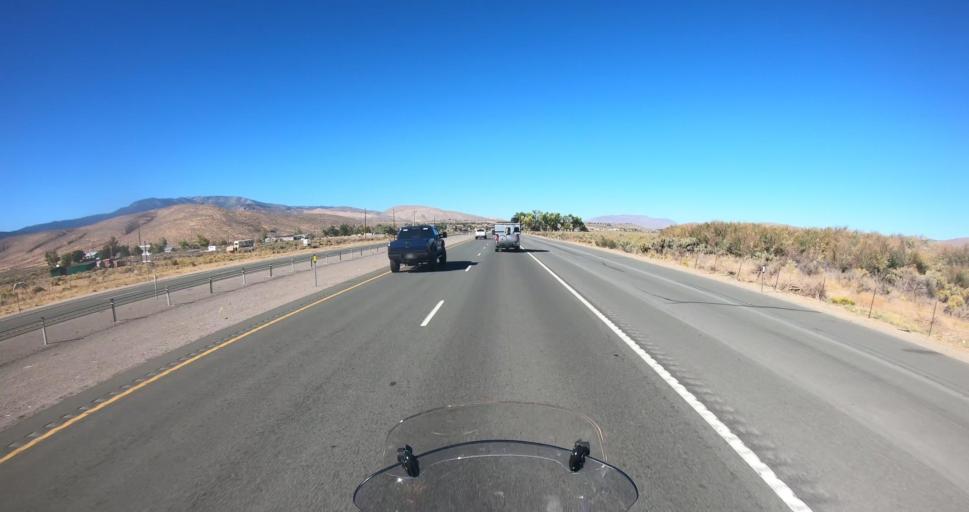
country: US
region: Nevada
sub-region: Douglas County
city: Indian Hills
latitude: 39.0528
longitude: -119.7798
